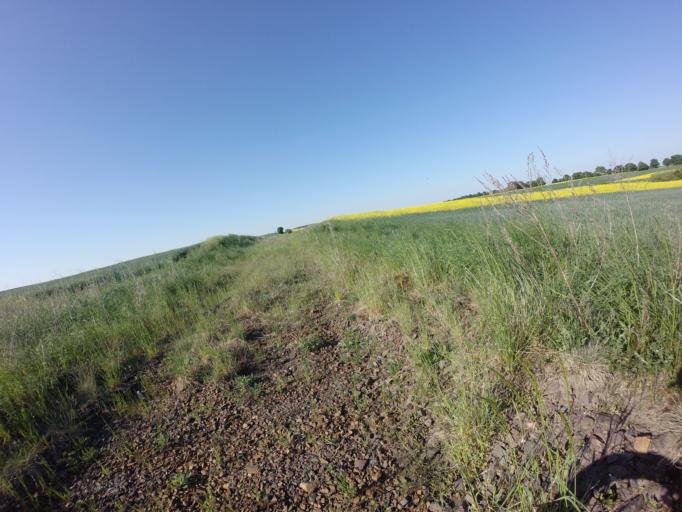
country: PL
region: West Pomeranian Voivodeship
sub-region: Powiat choszczenski
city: Choszczno
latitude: 53.1460
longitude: 15.3712
